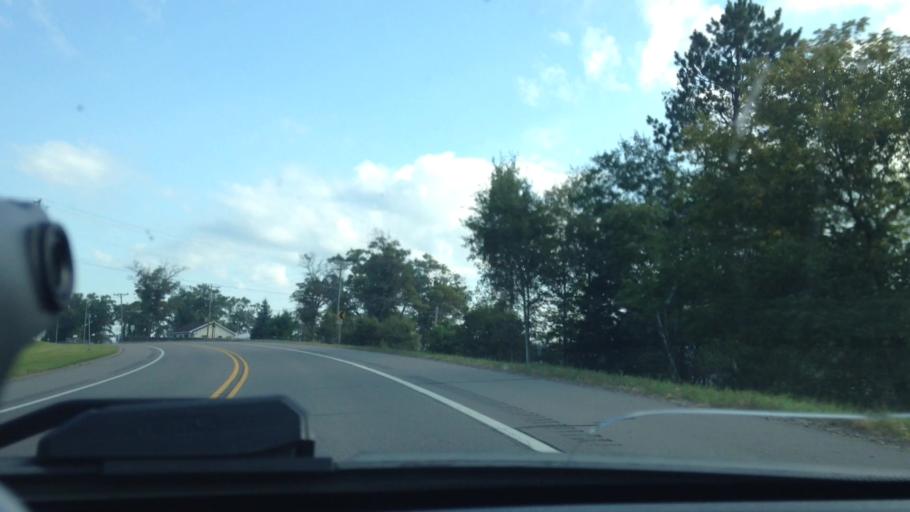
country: US
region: Michigan
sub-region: Dickinson County
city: Norway
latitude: 45.7702
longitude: -87.9095
